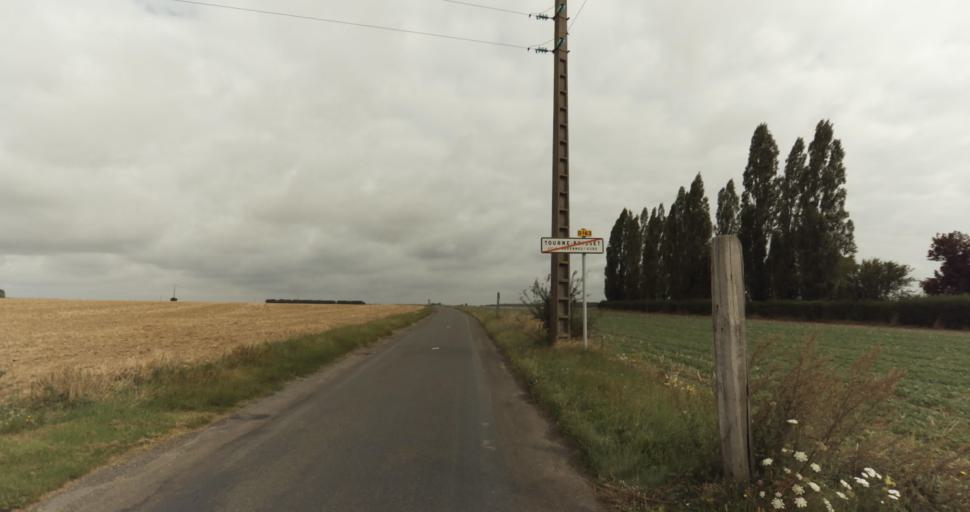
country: FR
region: Haute-Normandie
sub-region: Departement de l'Eure
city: La Couture-Boussey
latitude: 48.9138
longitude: 1.4066
